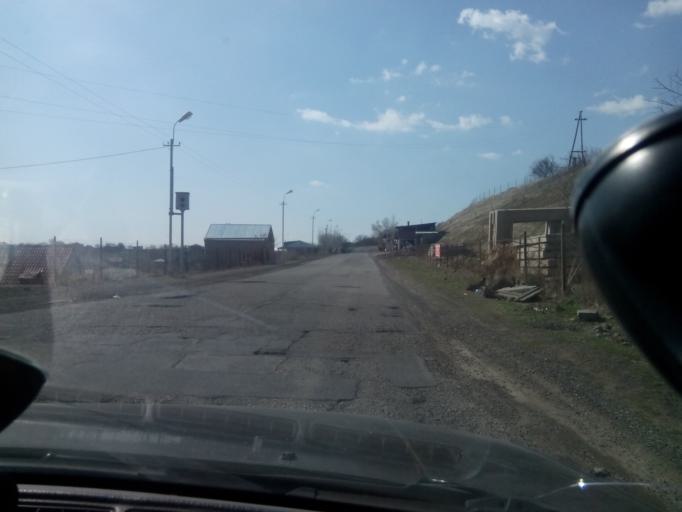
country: AM
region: Kotayk'i Marz
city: Goght'
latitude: 40.1361
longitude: 44.7730
